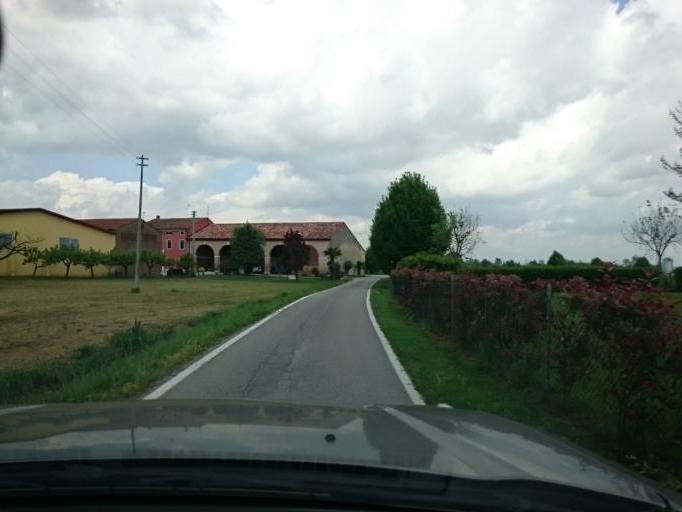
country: IT
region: Veneto
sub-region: Provincia di Vicenza
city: Villaganzerla
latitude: 45.4535
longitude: 11.6377
